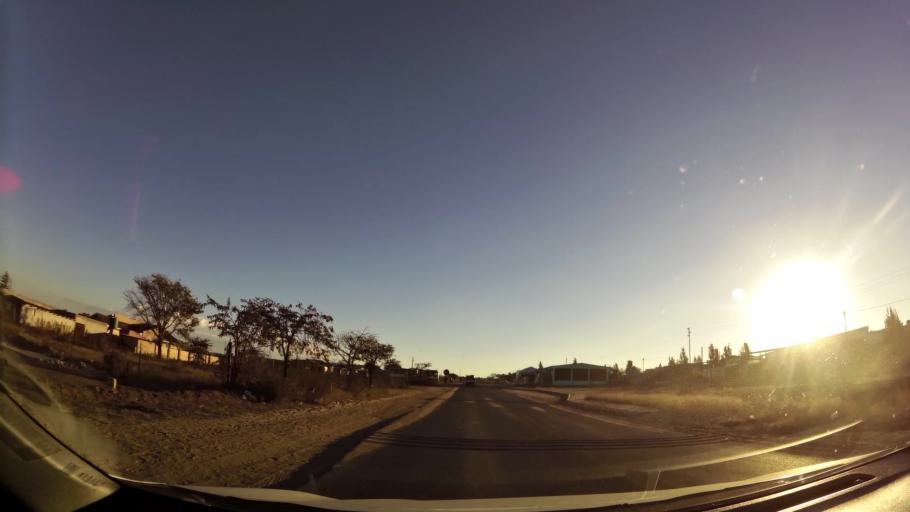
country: ZA
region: Limpopo
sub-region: Capricorn District Municipality
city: Polokwane
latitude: -23.8382
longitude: 29.3526
